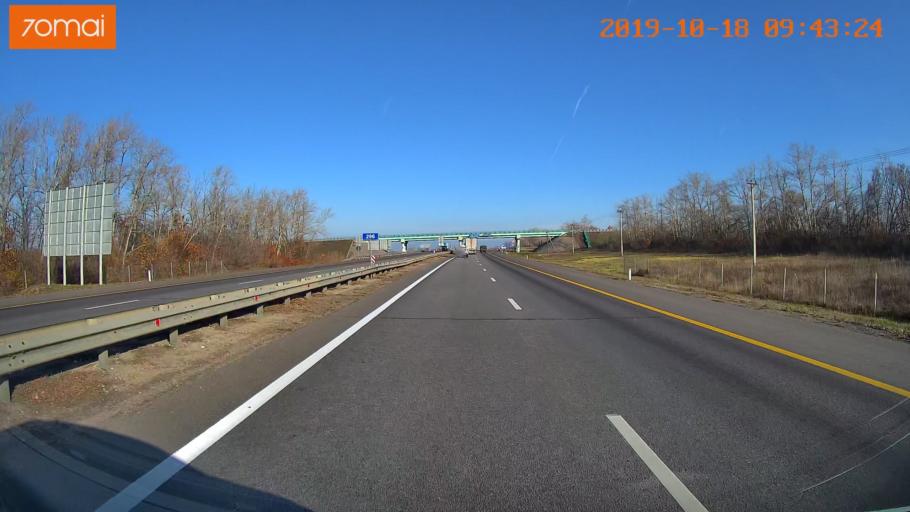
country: RU
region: Tula
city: Kazachka
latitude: 53.2971
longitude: 38.1781
